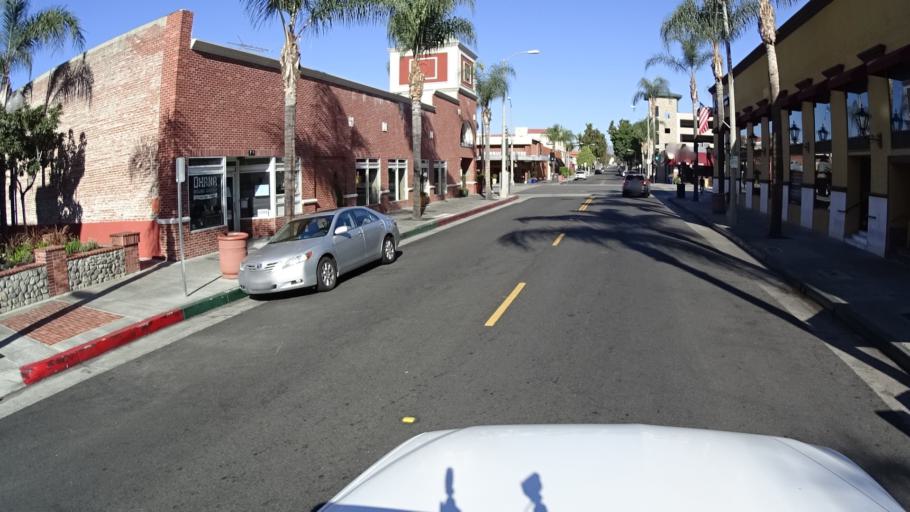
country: US
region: California
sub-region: Los Angeles County
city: Alhambra
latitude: 34.0942
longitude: -118.1277
